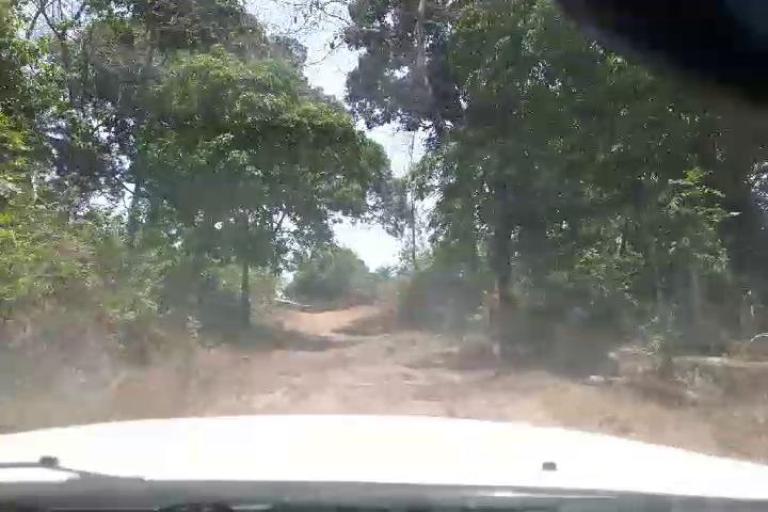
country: SL
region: Northern Province
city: Alikalia
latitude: 9.0718
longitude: -11.4830
